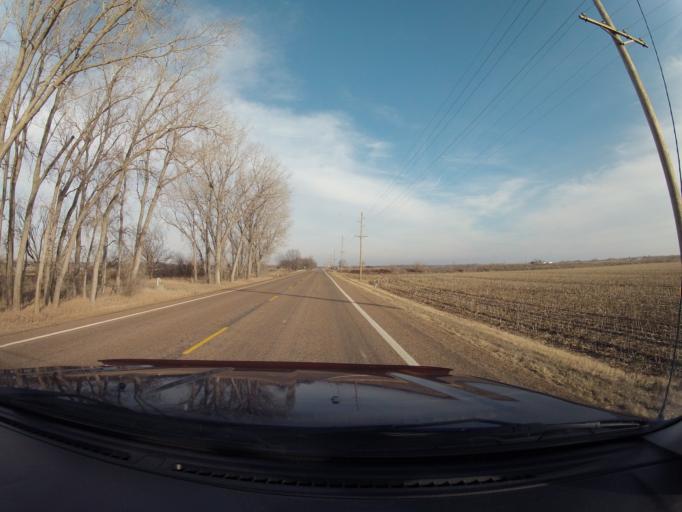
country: US
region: Kansas
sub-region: Pottawatomie County
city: Saint Marys
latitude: 39.2165
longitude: -96.1604
